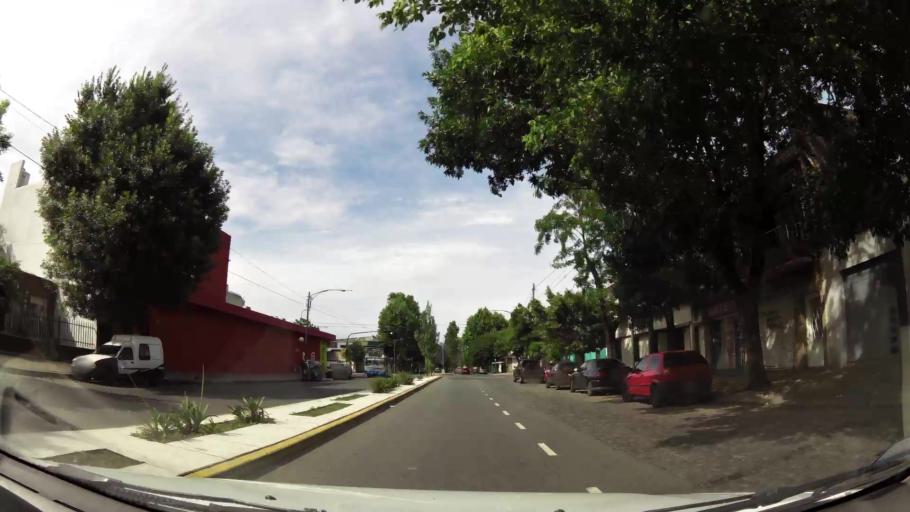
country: AR
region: Buenos Aires F.D.
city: Villa Lugano
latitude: -34.6655
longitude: -58.5037
